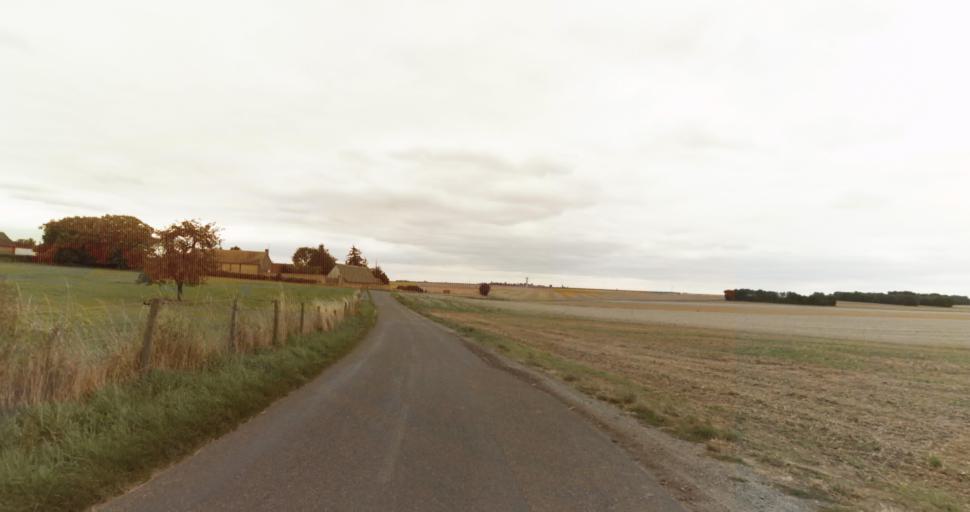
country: FR
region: Haute-Normandie
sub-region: Departement de l'Eure
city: Menilles
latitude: 48.9759
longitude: 1.2815
